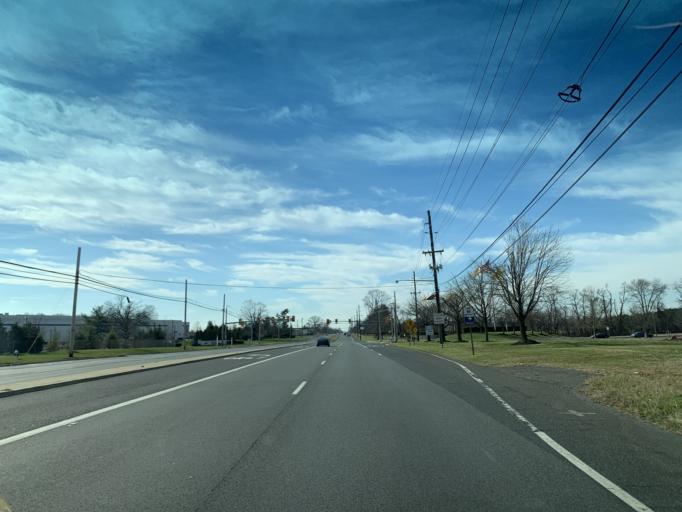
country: US
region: New Jersey
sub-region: Burlington County
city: Roebling
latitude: 40.0985
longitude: -74.8025
